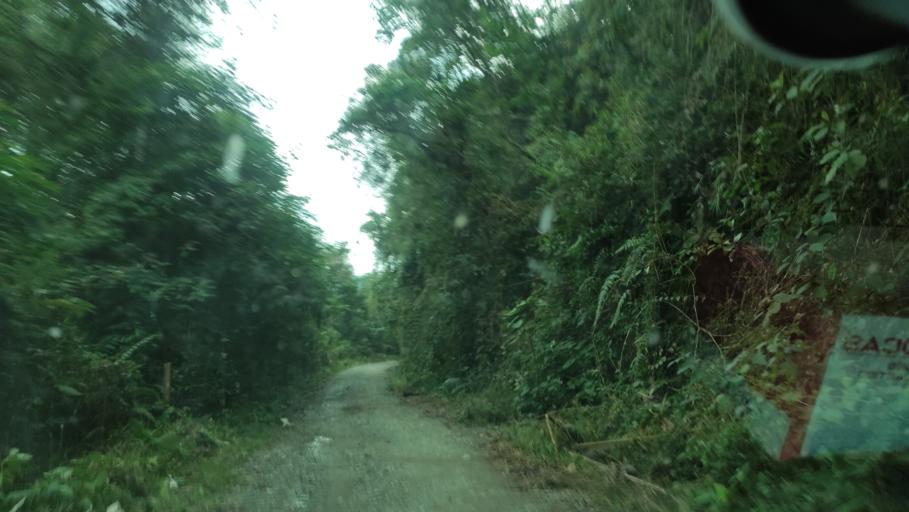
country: CO
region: Valle del Cauca
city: San Pedro
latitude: 3.8810
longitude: -76.1518
